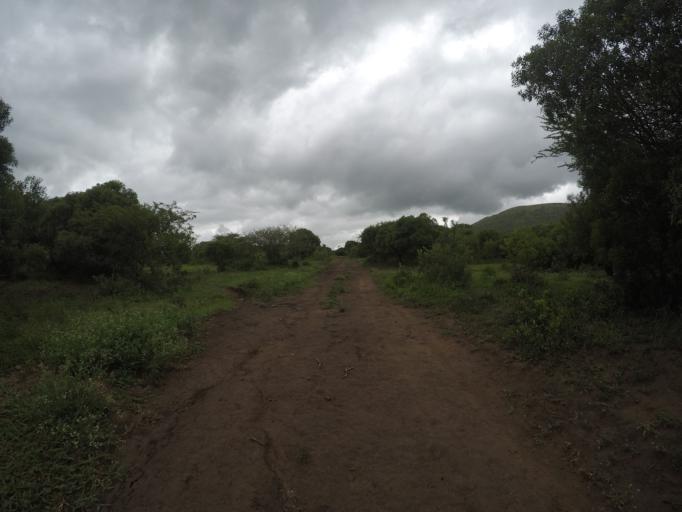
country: ZA
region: KwaZulu-Natal
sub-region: uThungulu District Municipality
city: Empangeni
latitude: -28.5689
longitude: 31.8714
